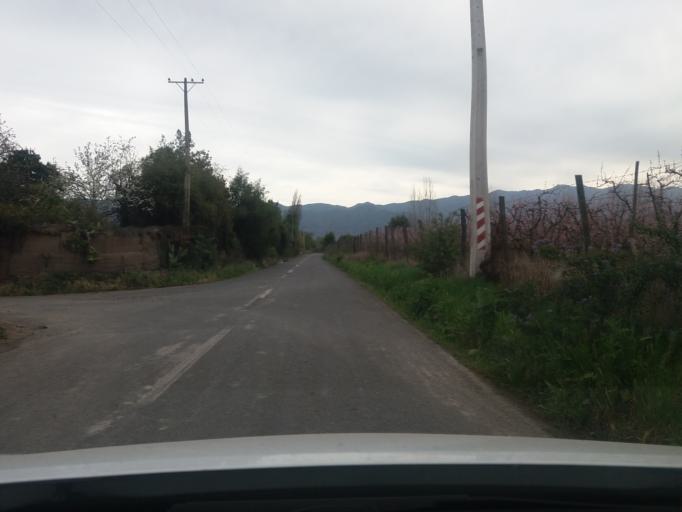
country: CL
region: Valparaiso
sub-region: Provincia de Los Andes
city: Los Andes
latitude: -32.8534
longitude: -70.6451
